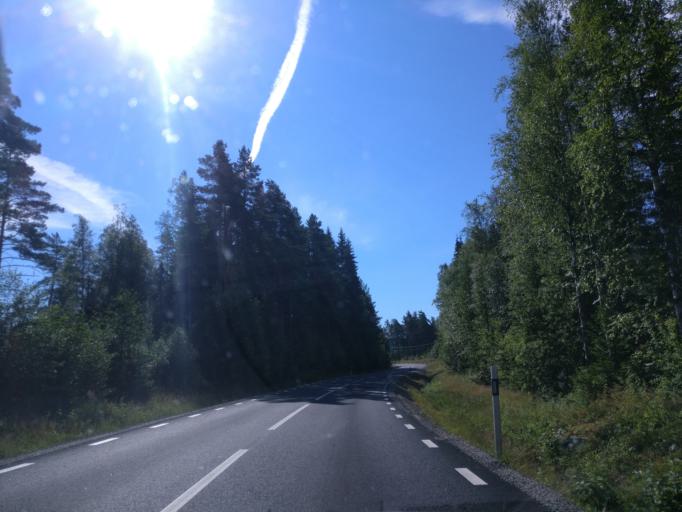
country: SE
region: Vaermland
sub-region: Hagfors Kommun
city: Hagfors
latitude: 60.0385
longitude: 13.8247
